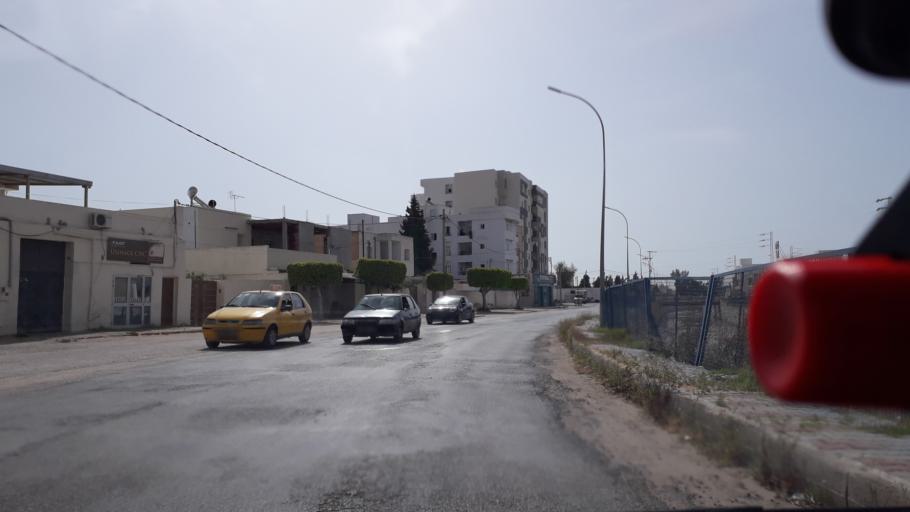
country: TN
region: Safaqis
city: Al Qarmadah
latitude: 34.8001
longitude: 10.7684
